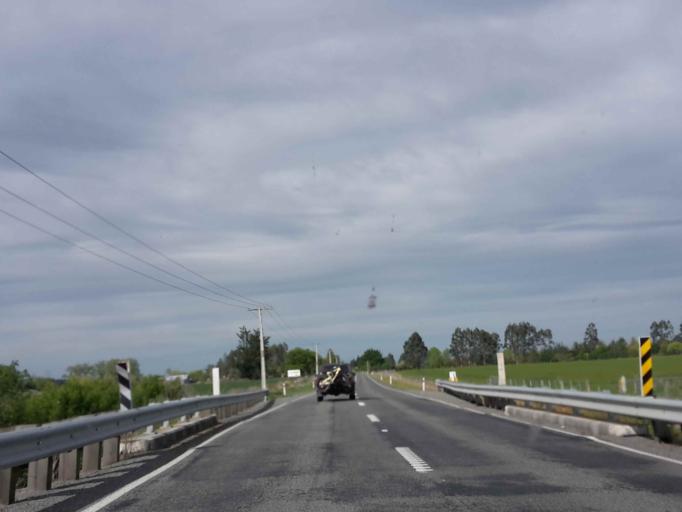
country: NZ
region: Canterbury
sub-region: Timaru District
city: Pleasant Point
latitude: -44.1190
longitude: 171.1999
